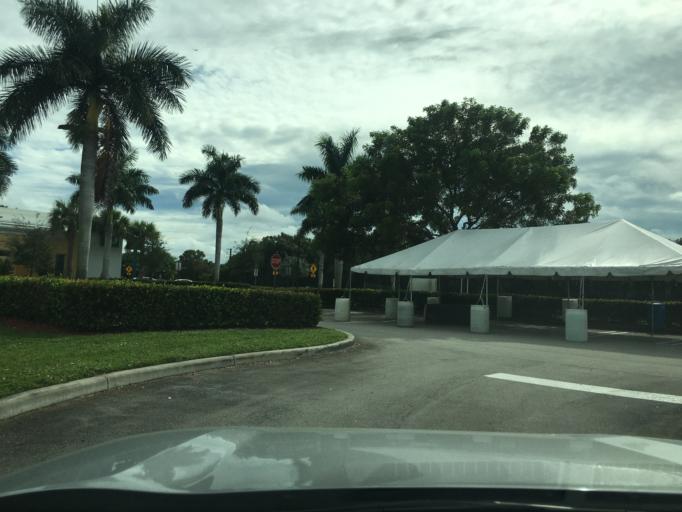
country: US
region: Florida
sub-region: Miami-Dade County
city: Palm Springs North
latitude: 25.9430
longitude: -80.3438
